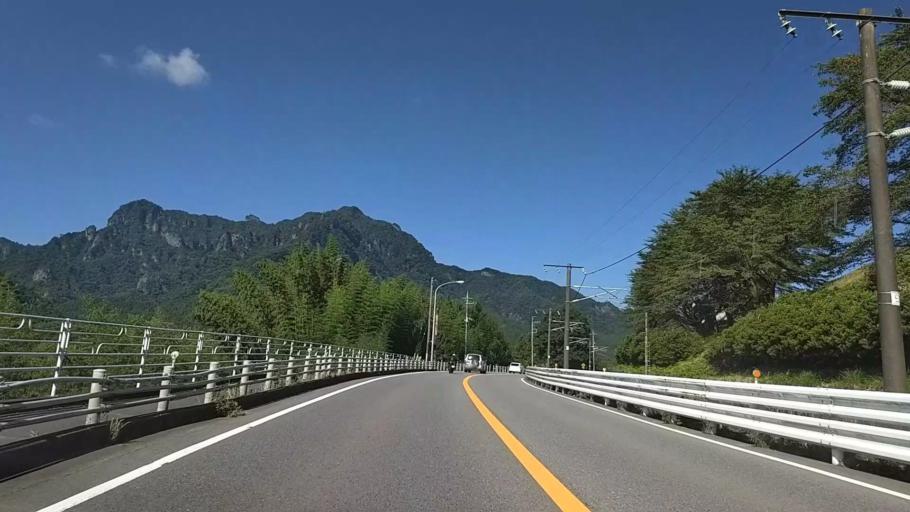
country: JP
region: Gunma
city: Annaka
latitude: 36.3256
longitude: 138.7607
